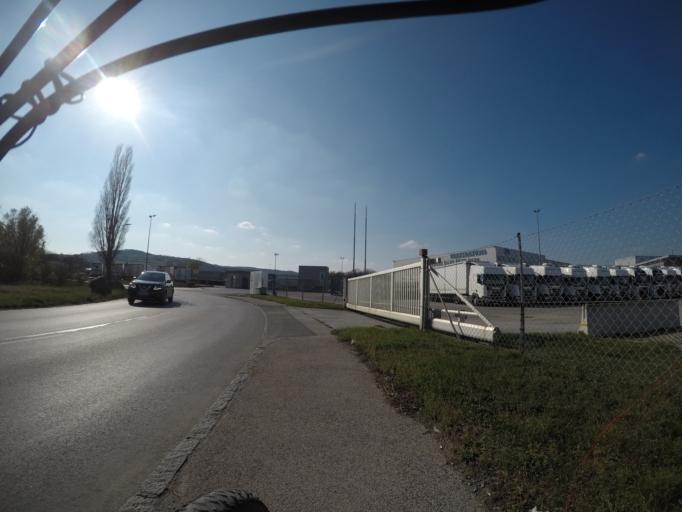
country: AT
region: Lower Austria
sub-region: Politischer Bezirk Modling
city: Neu-Guntramsdorf
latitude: 48.0692
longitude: 16.3156
